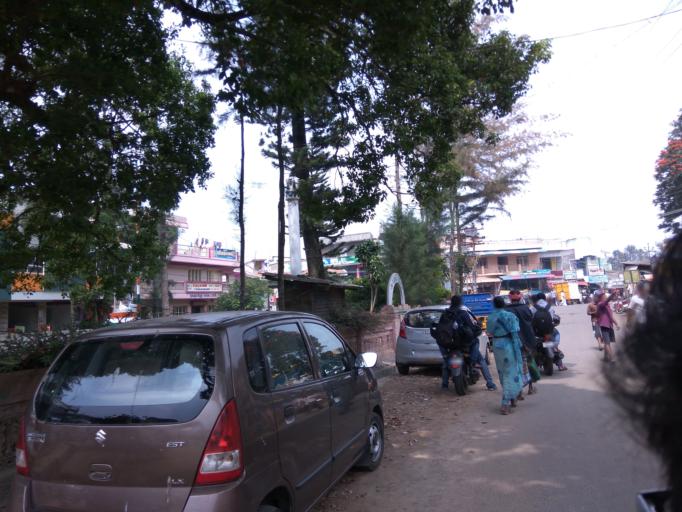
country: IN
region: Tamil Nadu
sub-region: Salem
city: Salem
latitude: 11.7739
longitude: 78.2098
